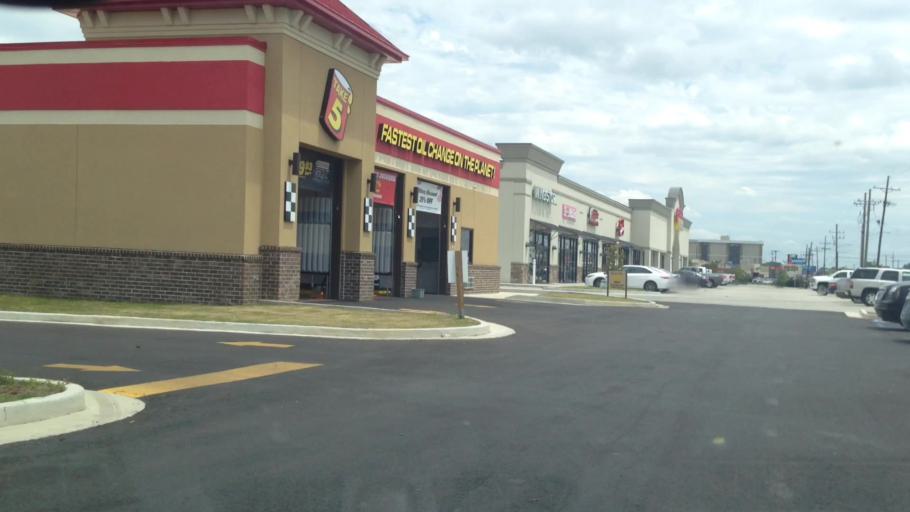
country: US
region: Louisiana
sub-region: Iberia Parish
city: New Iberia
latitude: 29.9883
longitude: -91.8255
